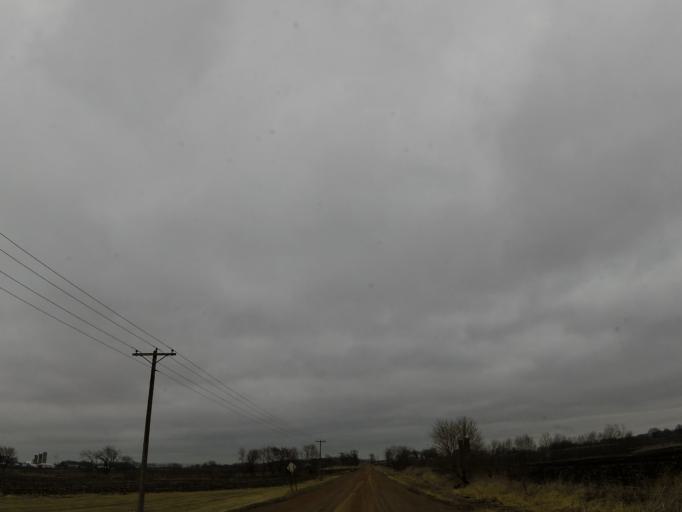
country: US
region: Minnesota
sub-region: Scott County
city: Jordan
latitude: 44.7033
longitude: -93.5393
